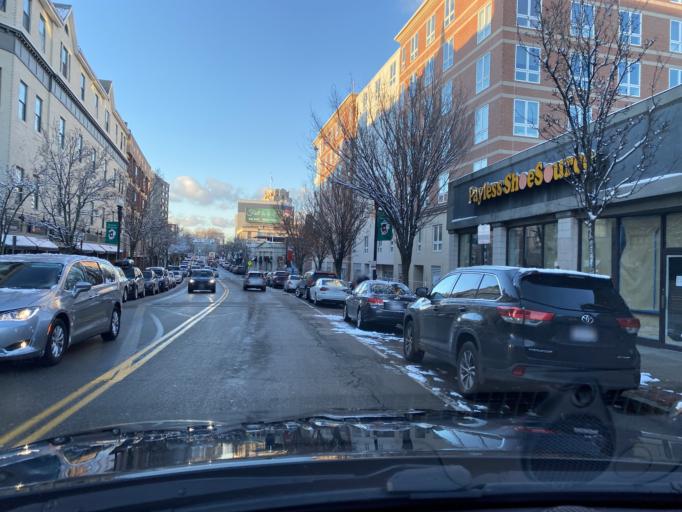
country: US
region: Massachusetts
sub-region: Norfolk County
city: Quincy
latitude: 42.2475
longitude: -71.0011
